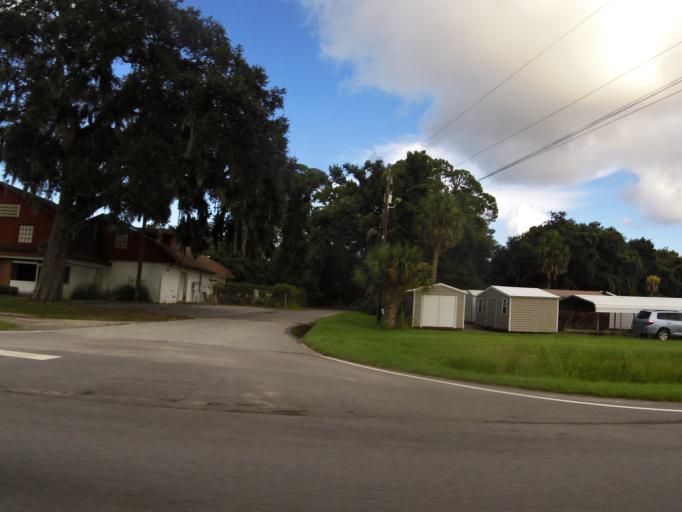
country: US
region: Georgia
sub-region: Glynn County
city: Country Club Estates
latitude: 31.1905
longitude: -81.4692
